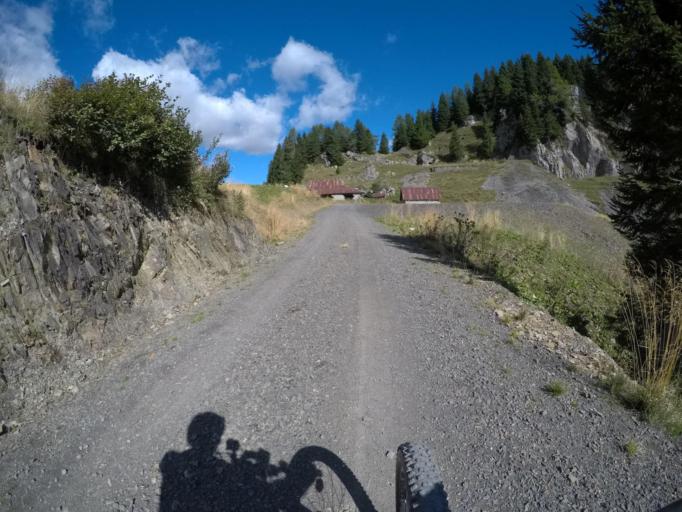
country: IT
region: Friuli Venezia Giulia
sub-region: Provincia di Udine
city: Ligosullo
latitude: 46.5730
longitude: 13.0951
